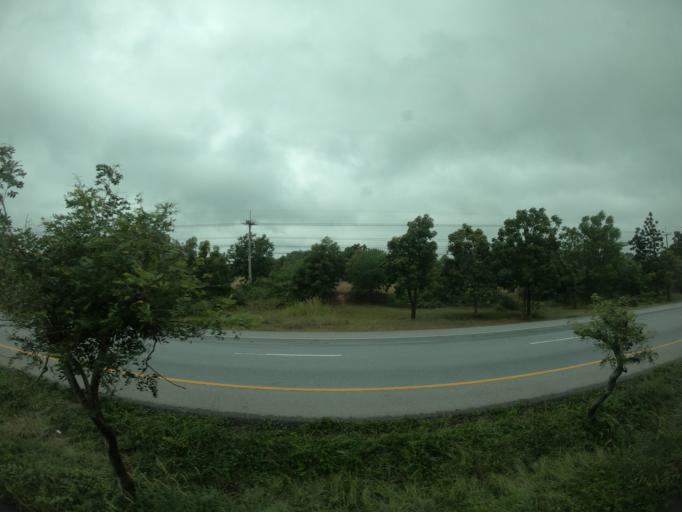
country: TH
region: Nakhon Ratchasima
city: Non Daeng
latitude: 15.4305
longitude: 102.4885
